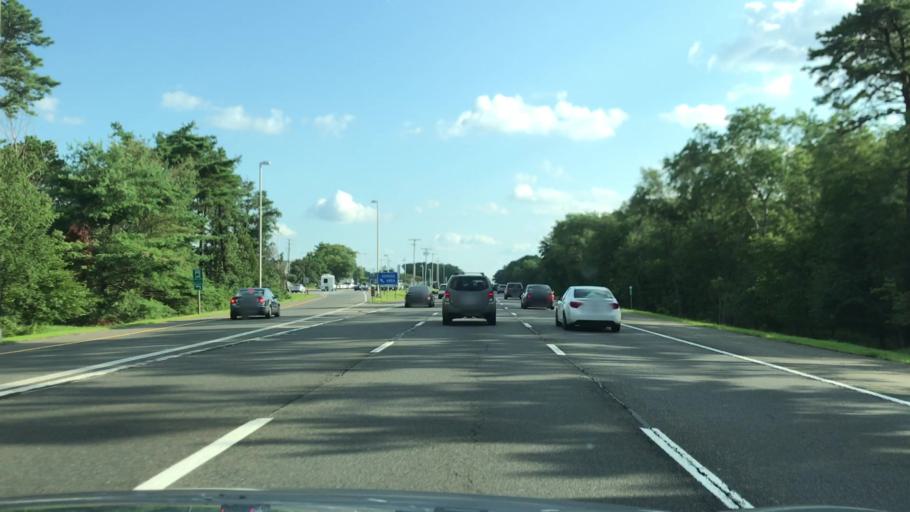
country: US
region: New Jersey
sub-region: Ocean County
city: Forked River
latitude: 39.8764
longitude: -74.2145
